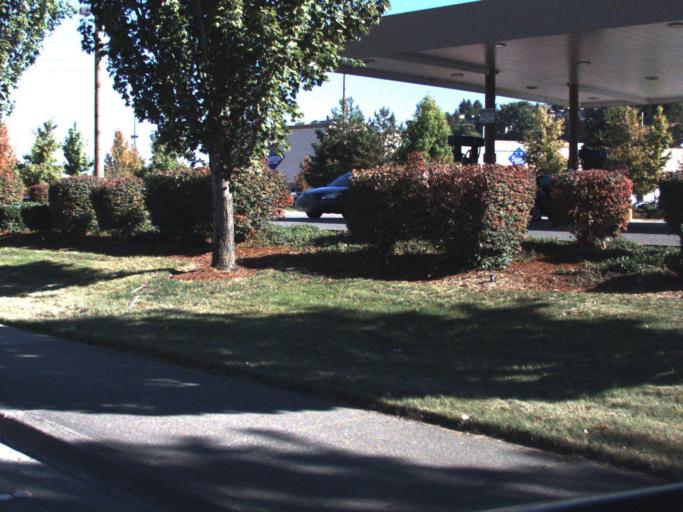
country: US
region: Washington
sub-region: King County
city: Renton
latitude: 47.4716
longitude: -122.2079
